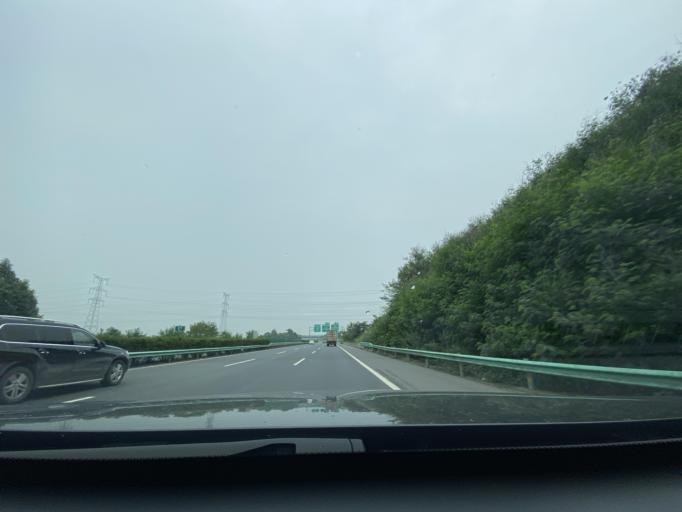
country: CN
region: Sichuan
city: Longquan
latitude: 30.3330
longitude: 104.1196
